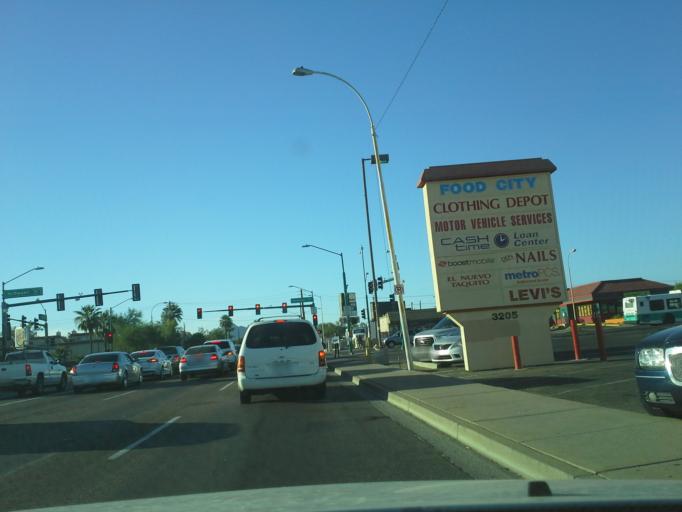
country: US
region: Arizona
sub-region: Maricopa County
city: Phoenix
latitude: 33.4651
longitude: -112.0128
